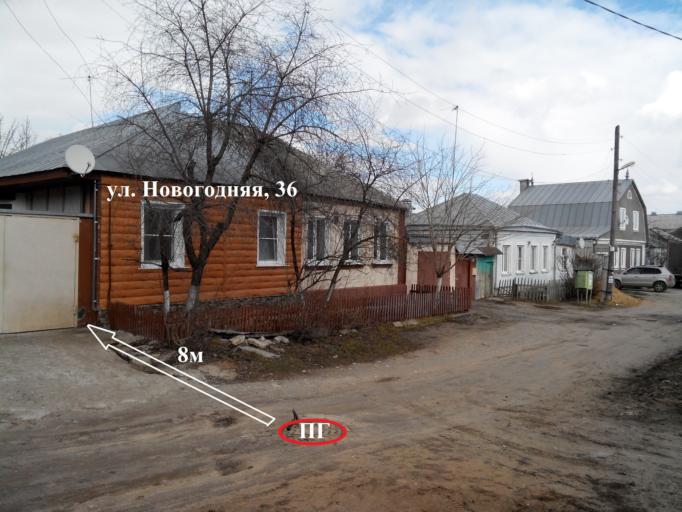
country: RU
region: Voronezj
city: Voronezh
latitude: 51.6360
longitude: 39.1574
